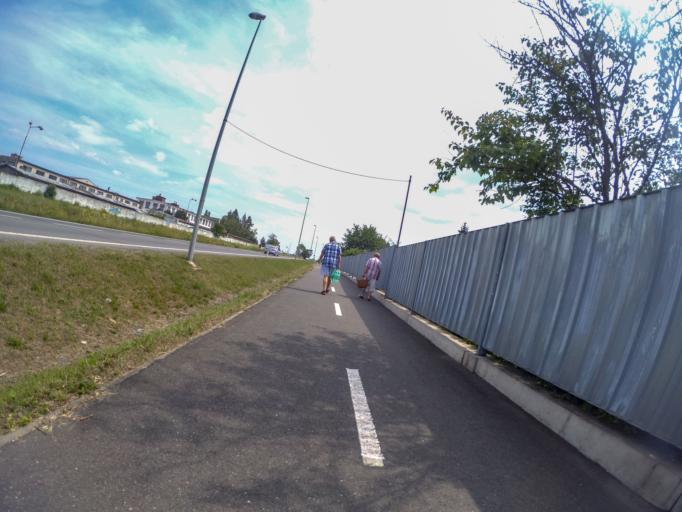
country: CZ
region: Praha
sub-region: Praha 19
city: Kbely
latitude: 50.1301
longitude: 14.5397
